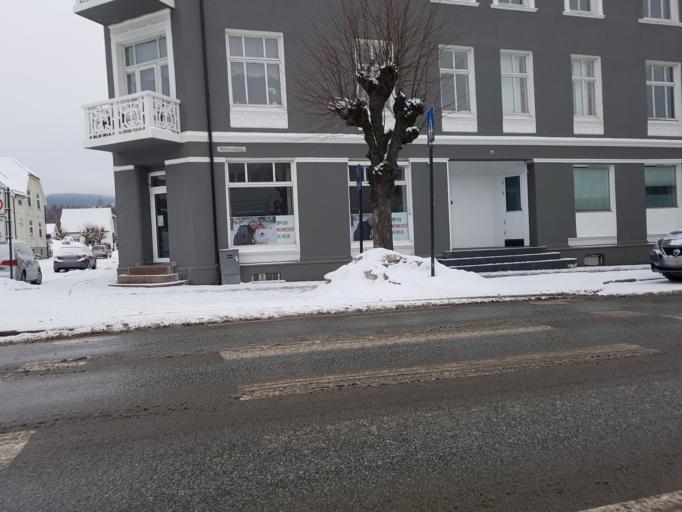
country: NO
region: Buskerud
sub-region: Drammen
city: Drammen
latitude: 59.7383
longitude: 10.1927
